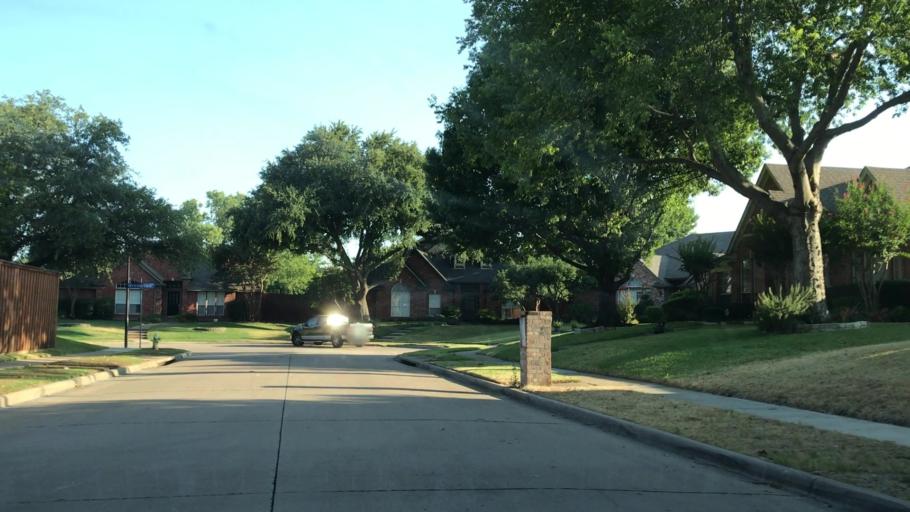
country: US
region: Texas
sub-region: Dallas County
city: Coppell
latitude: 32.9642
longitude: -96.9973
